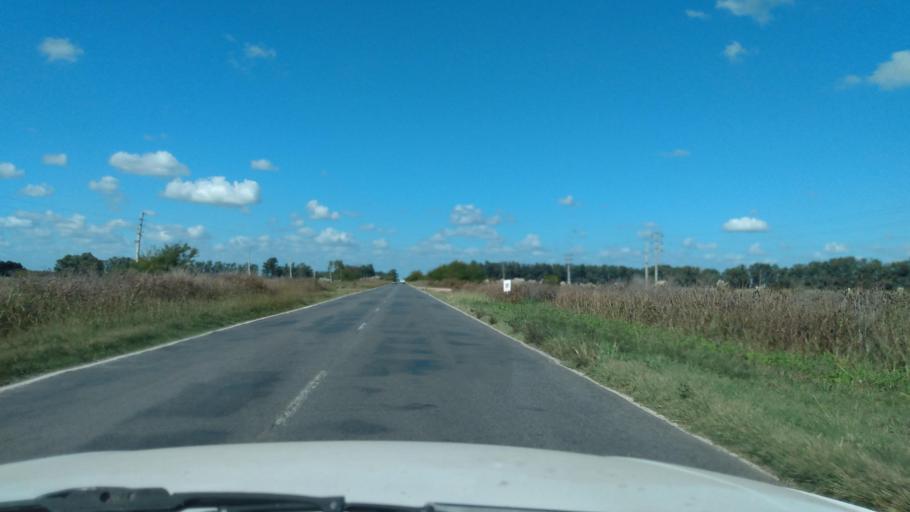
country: AR
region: Buenos Aires
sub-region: Partido de Mercedes
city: Mercedes
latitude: -34.7314
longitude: -59.3896
